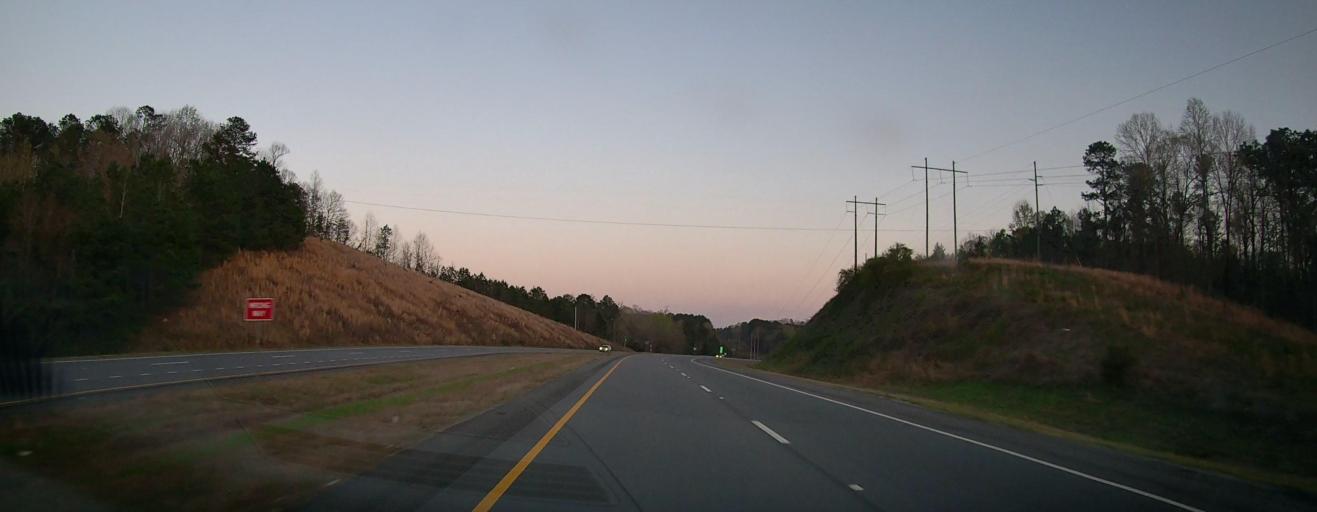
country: US
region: Alabama
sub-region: Tallapoosa County
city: Alexander City
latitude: 32.8966
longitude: -85.8810
